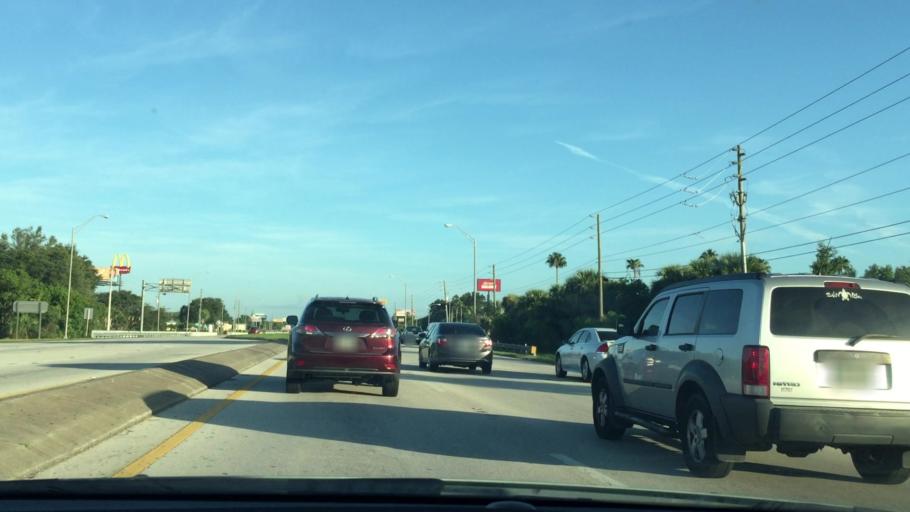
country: US
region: Florida
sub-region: Osceola County
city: Buenaventura Lakes
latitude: 28.2872
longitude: -81.3558
